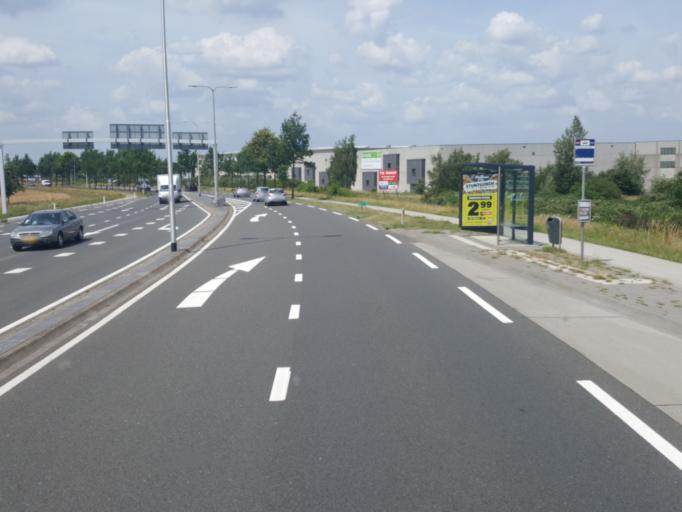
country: NL
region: Limburg
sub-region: Gemeente Peel en Maas
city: Maasbree
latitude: 51.3966
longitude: 6.0834
